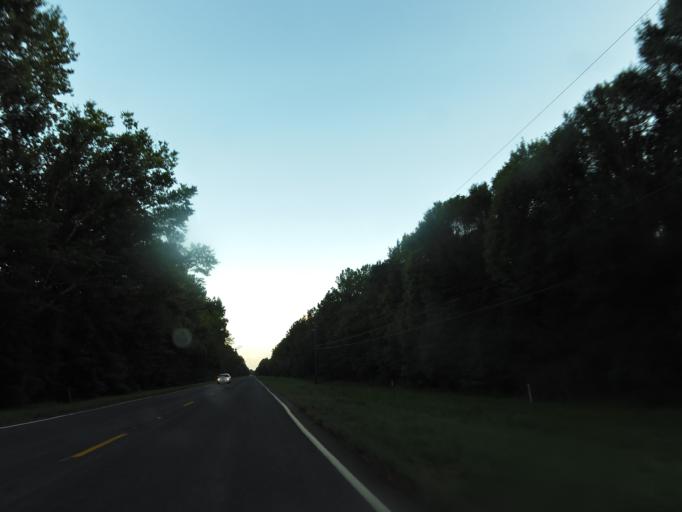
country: US
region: Georgia
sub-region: Camden County
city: Woodbine
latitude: 30.9909
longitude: -81.7296
